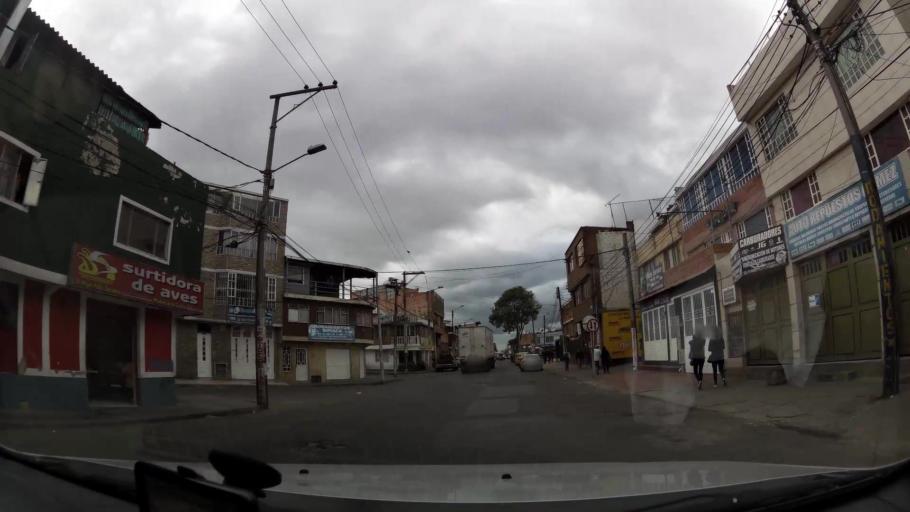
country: CO
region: Bogota D.C.
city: Bogota
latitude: 4.5965
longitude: -74.1414
